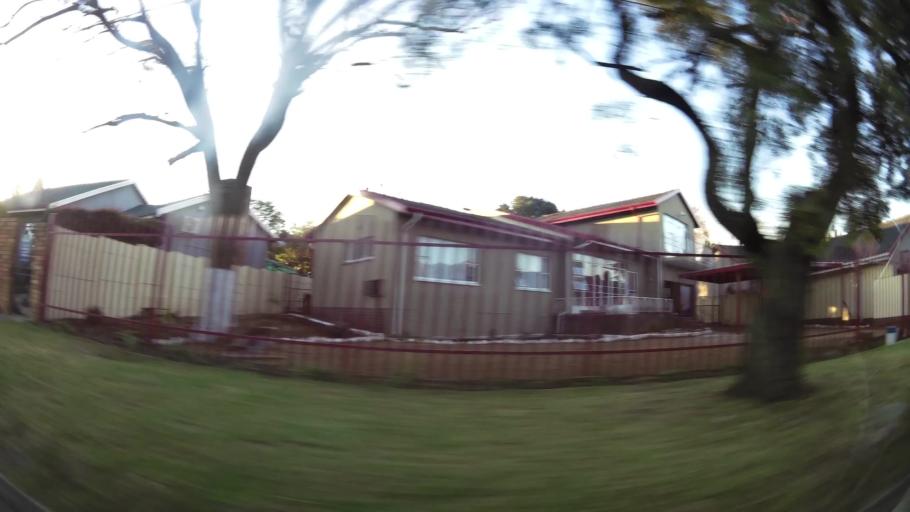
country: ZA
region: Gauteng
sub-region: City of Johannesburg Metropolitan Municipality
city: Roodepoort
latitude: -26.1486
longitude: 27.8909
